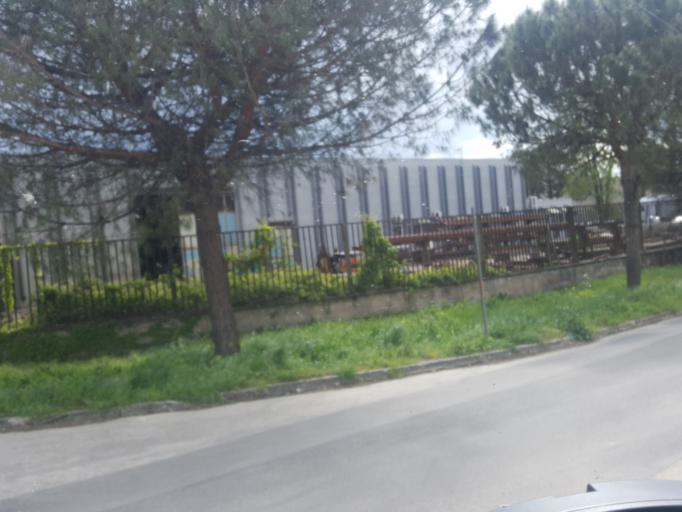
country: IT
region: Campania
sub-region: Provincia di Napoli
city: Torretta-Scalzapecora
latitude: 40.9348
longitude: 14.1120
